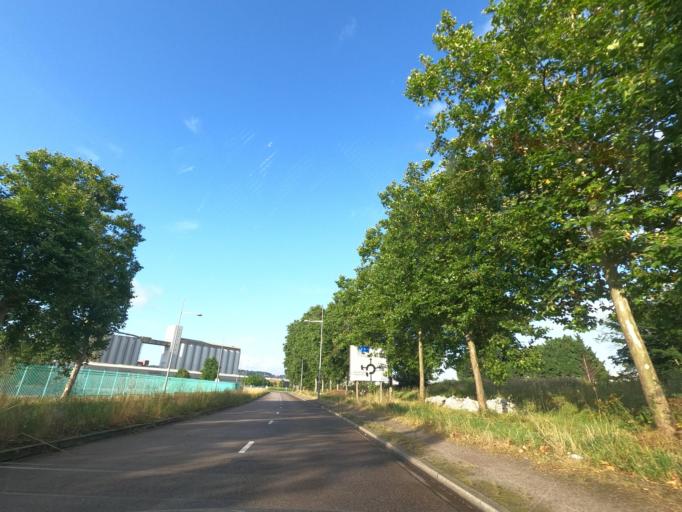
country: FR
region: Haute-Normandie
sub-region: Departement de la Seine-Maritime
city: Canteleu
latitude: 49.4353
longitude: 1.0492
